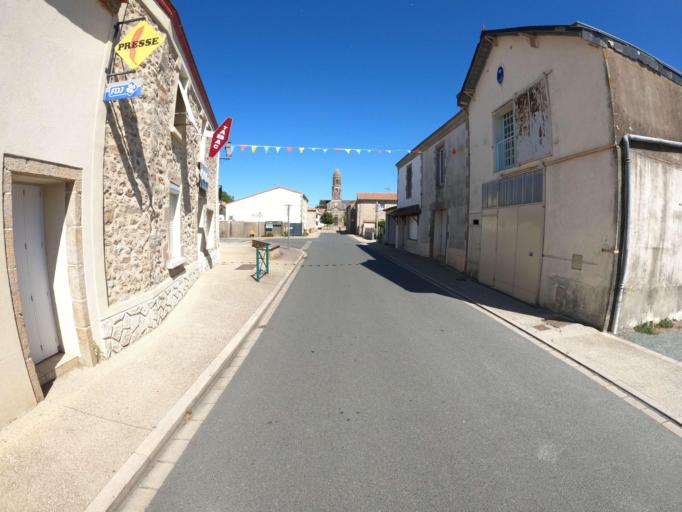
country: FR
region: Pays de la Loire
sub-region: Departement de la Vendee
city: Saint-Aubin-des-Ormeaux
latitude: 46.9738
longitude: -1.0524
